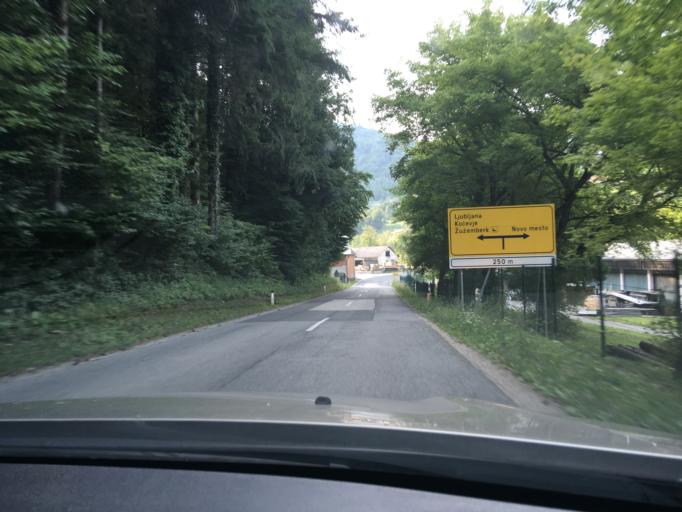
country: SI
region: Dolenjske Toplice
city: Dolenjske Toplice
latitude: 45.7775
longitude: 15.0194
